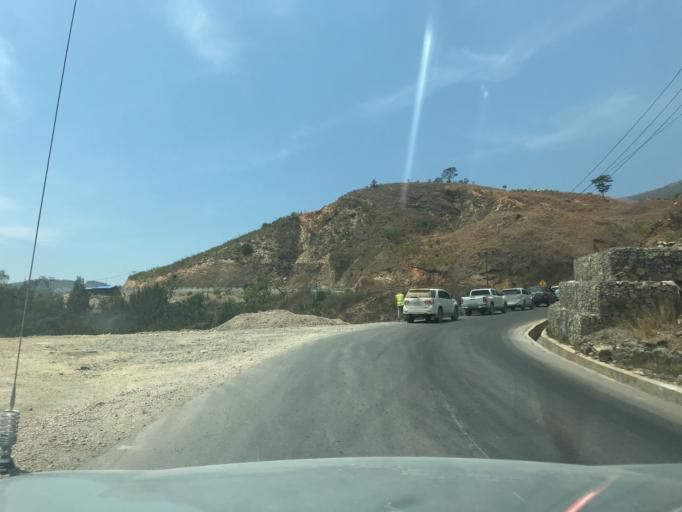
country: TL
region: Aileu
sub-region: Aileu Villa
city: Aileu
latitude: -8.8067
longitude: 125.5969
